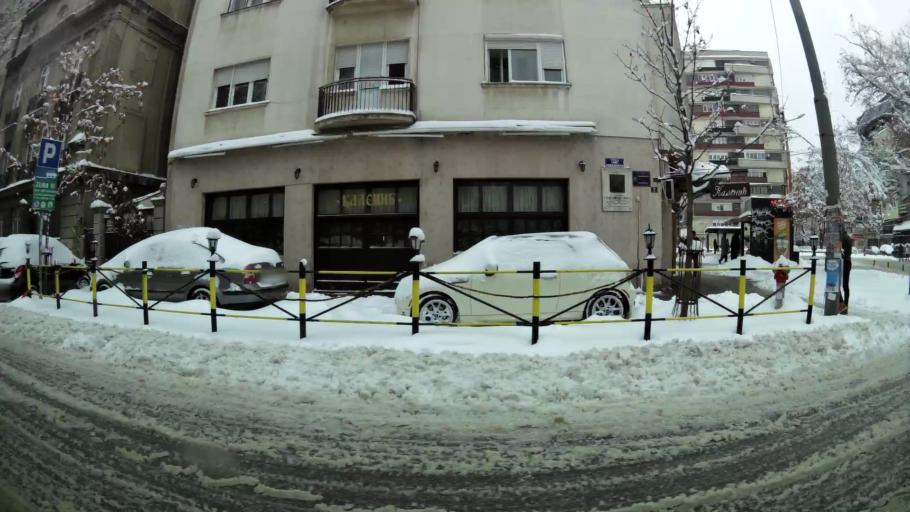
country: RS
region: Central Serbia
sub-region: Belgrade
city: Vracar
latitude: 44.8015
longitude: 20.4761
